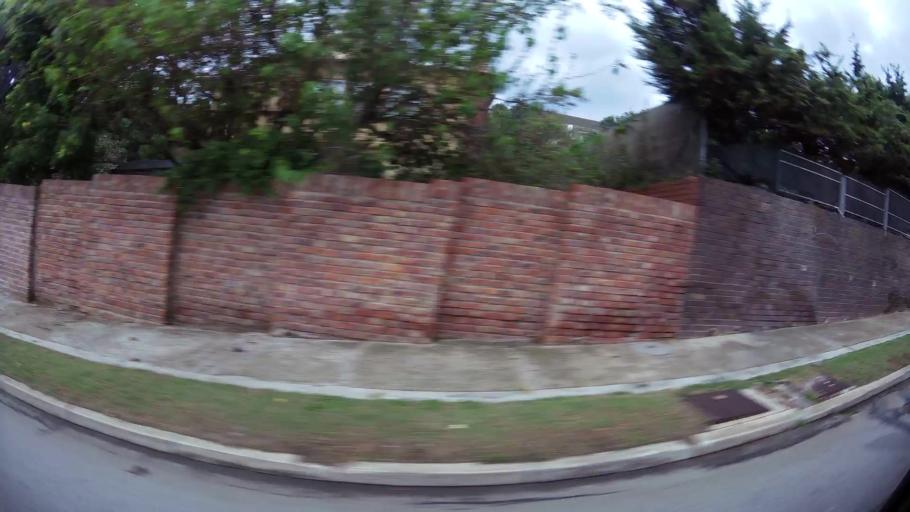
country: ZA
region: Eastern Cape
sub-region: Nelson Mandela Bay Metropolitan Municipality
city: Port Elizabeth
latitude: -33.9504
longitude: 25.5996
